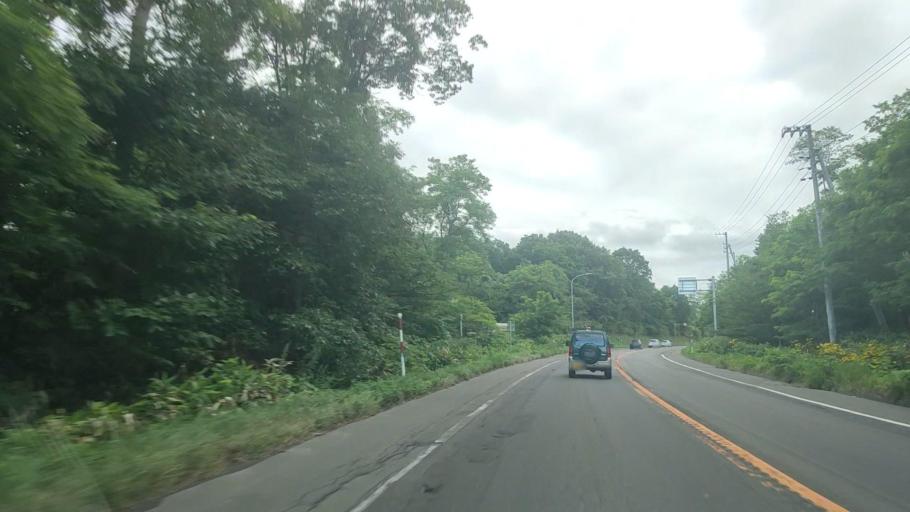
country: JP
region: Hokkaido
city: Nanae
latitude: 42.0652
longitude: 140.6027
